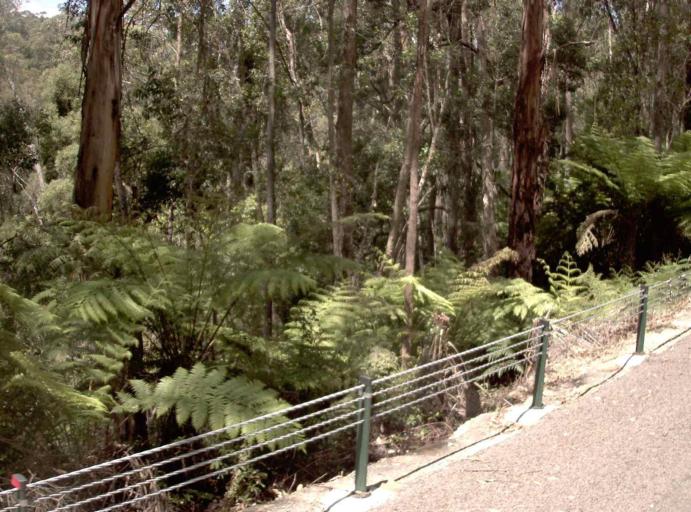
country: AU
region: New South Wales
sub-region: Bombala
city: Bombala
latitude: -37.5836
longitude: 148.9288
